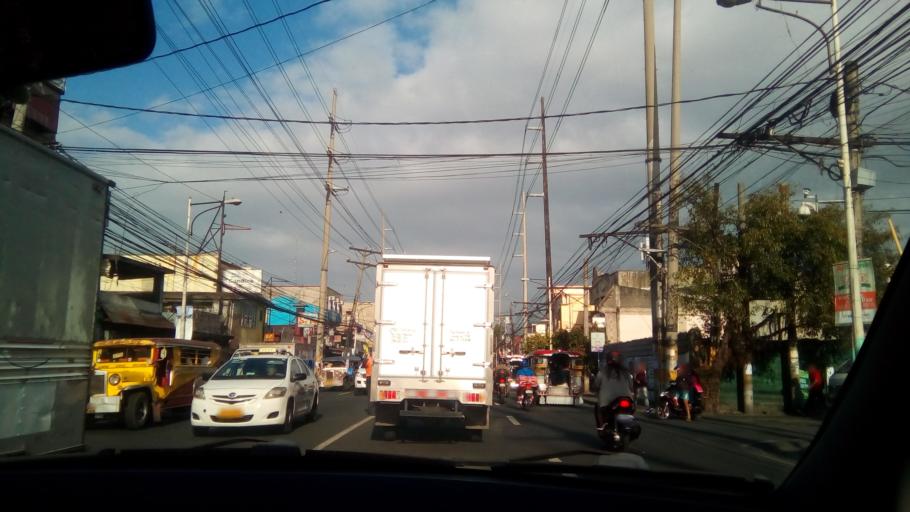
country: PH
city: Sambayanihan People's Village
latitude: 14.4380
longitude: 121.0047
